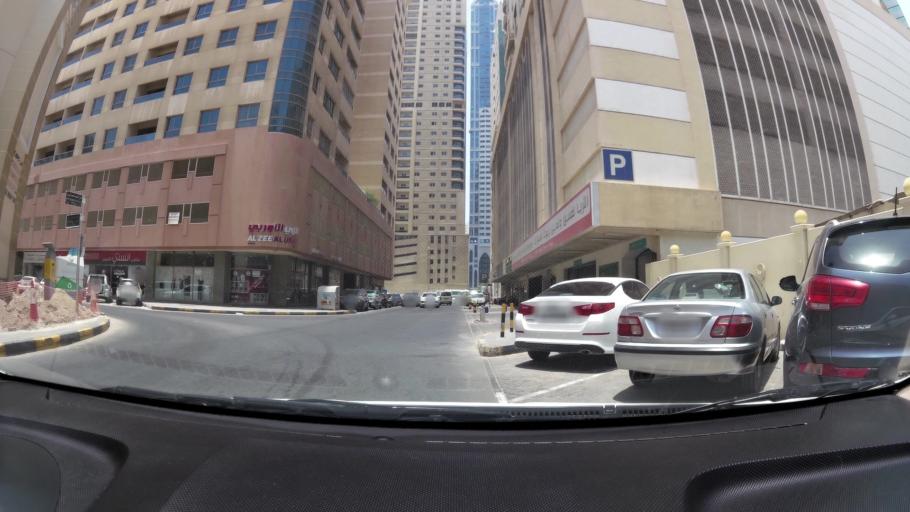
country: AE
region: Ash Shariqah
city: Sharjah
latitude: 25.3226
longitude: 55.3816
